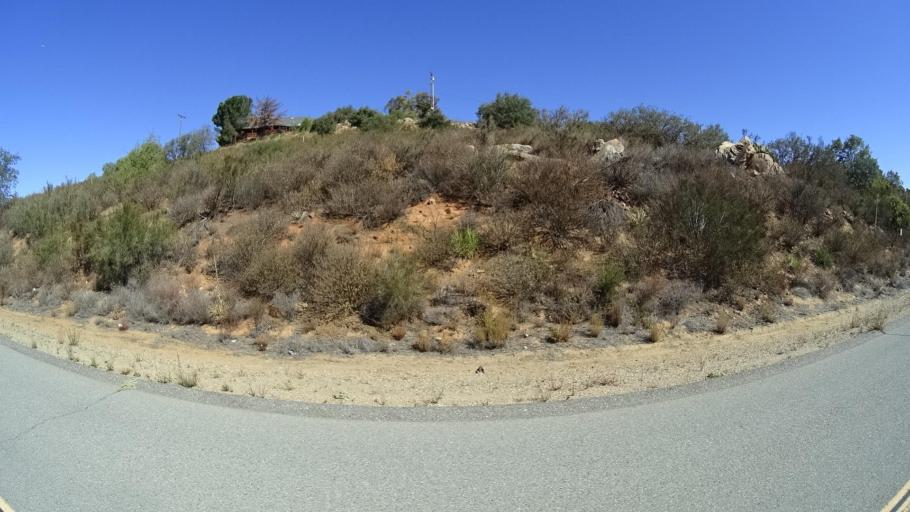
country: US
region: California
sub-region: San Diego County
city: Descanso
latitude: 32.7899
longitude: -116.6664
